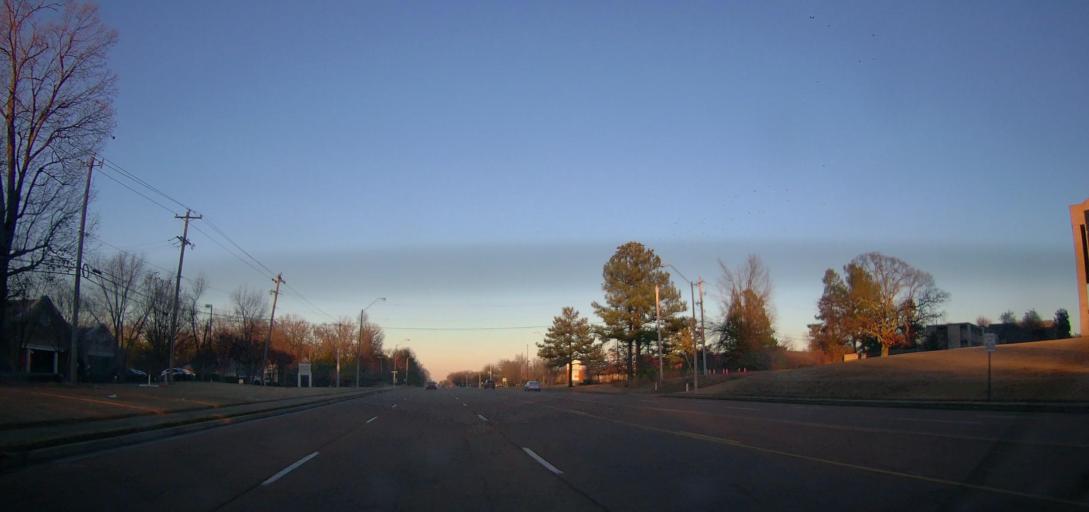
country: US
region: Tennessee
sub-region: Shelby County
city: Bartlett
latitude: 35.2301
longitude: -89.9004
